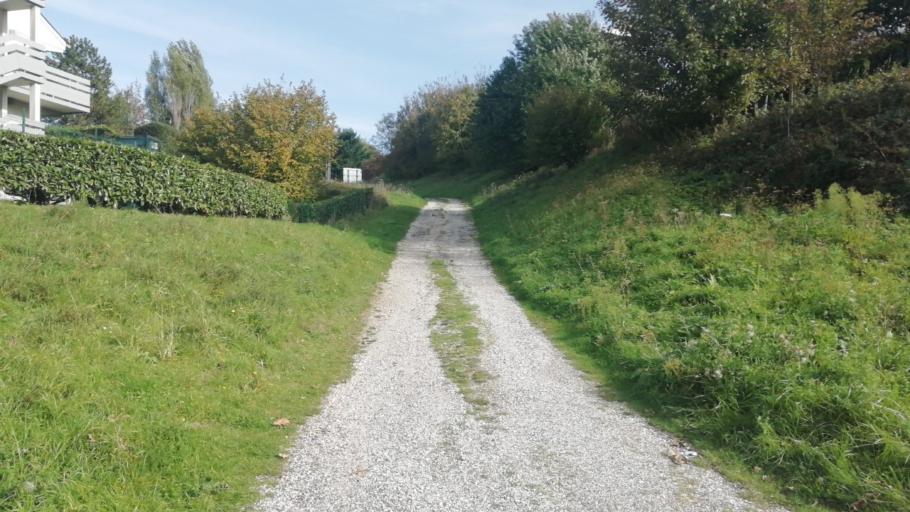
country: FR
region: Haute-Normandie
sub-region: Departement de la Seine-Maritime
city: Montivilliers
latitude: 49.5338
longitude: 0.1871
